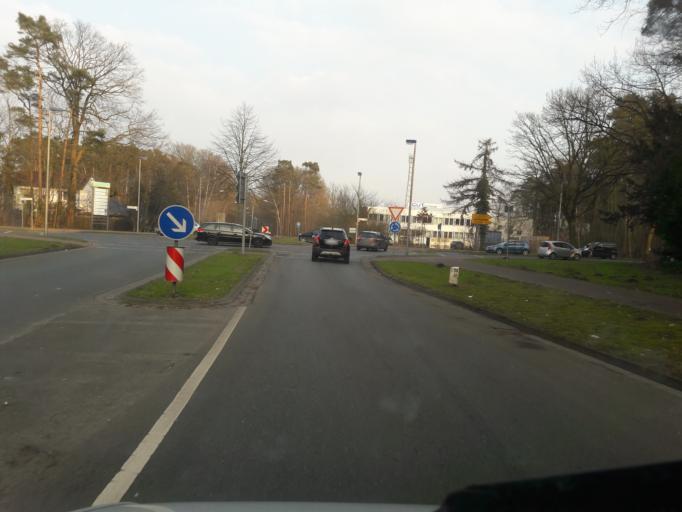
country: DE
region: North Rhine-Westphalia
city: Espelkamp
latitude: 52.3720
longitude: 8.6348
